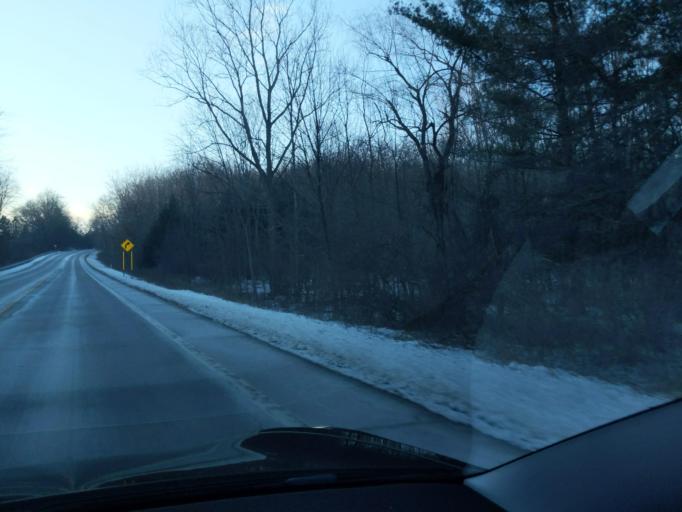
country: US
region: Michigan
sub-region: Ingham County
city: Mason
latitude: 42.5560
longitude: -84.3647
